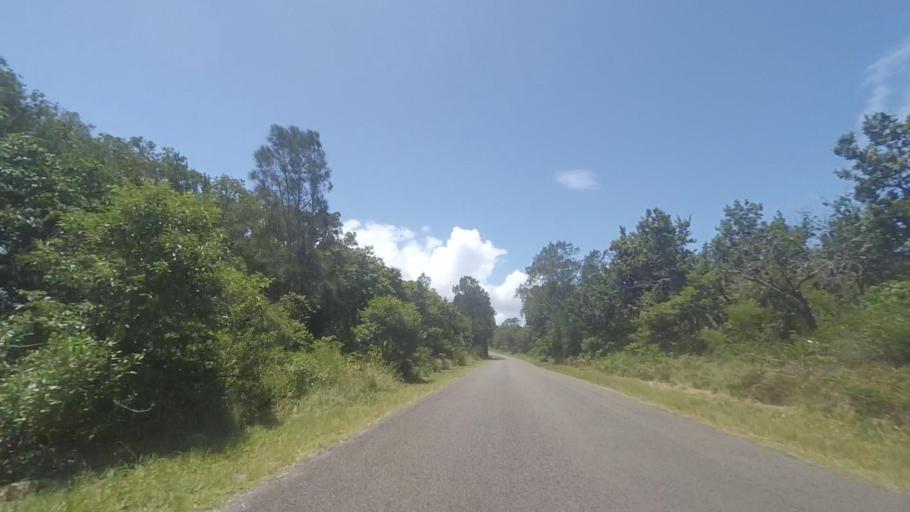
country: AU
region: New South Wales
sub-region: Great Lakes
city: Bulahdelah
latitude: -32.5357
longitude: 152.3198
